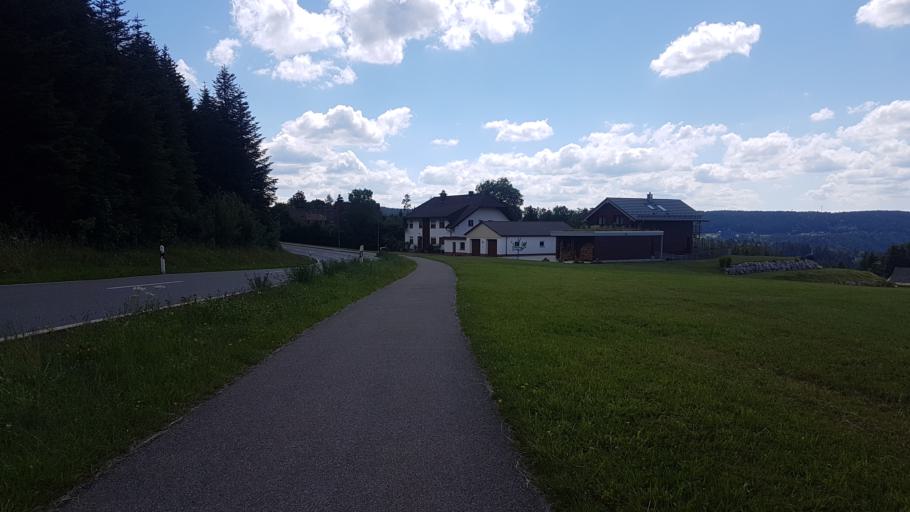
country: DE
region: Baden-Wuerttemberg
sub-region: Freiburg Region
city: Hardt
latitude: 48.2120
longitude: 8.4147
